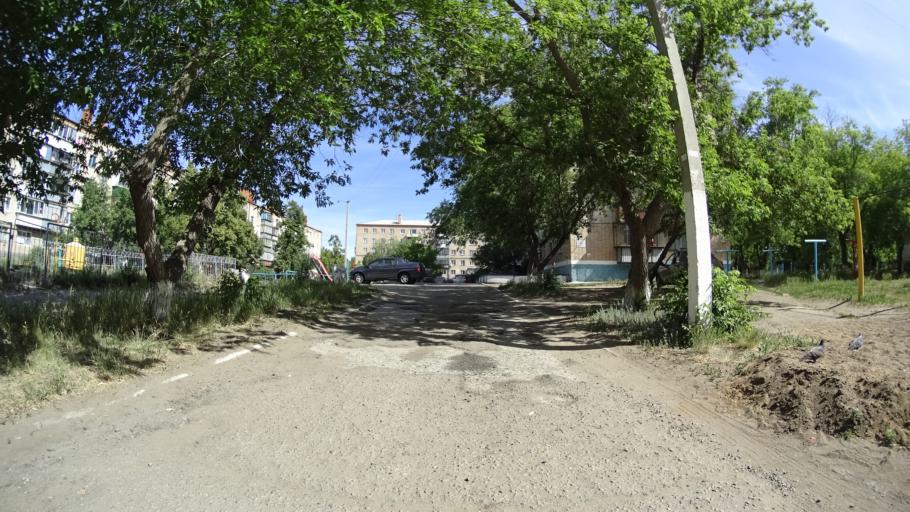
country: RU
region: Chelyabinsk
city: Troitsk
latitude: 54.0503
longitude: 61.6344
